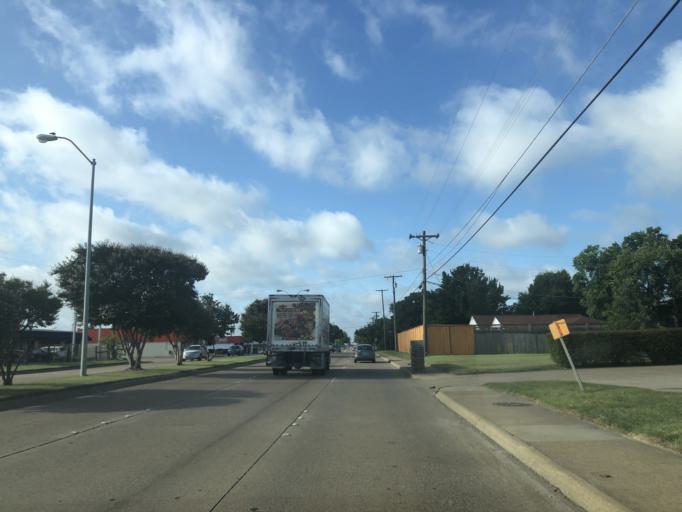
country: US
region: Texas
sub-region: Dallas County
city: Duncanville
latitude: 32.6711
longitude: -96.9087
